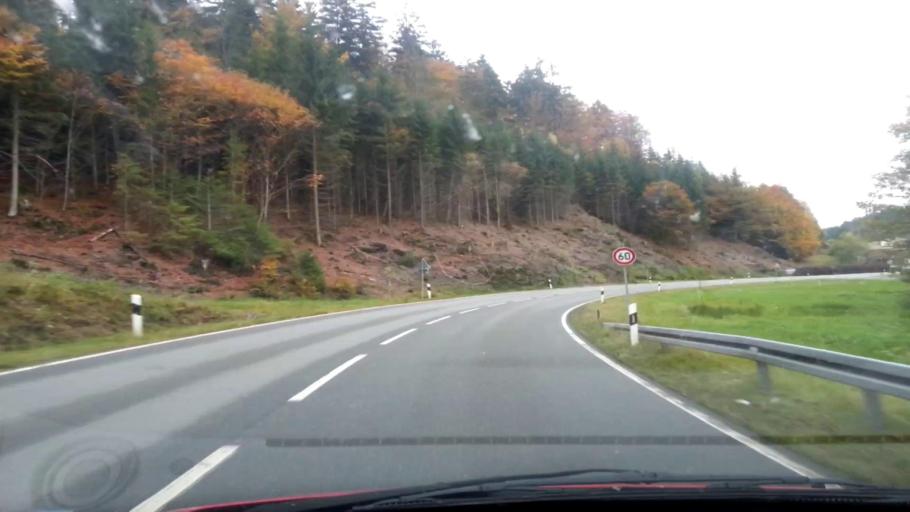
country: DE
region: Bavaria
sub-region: Upper Franconia
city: Warmensteinach
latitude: 49.9832
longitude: 11.7664
